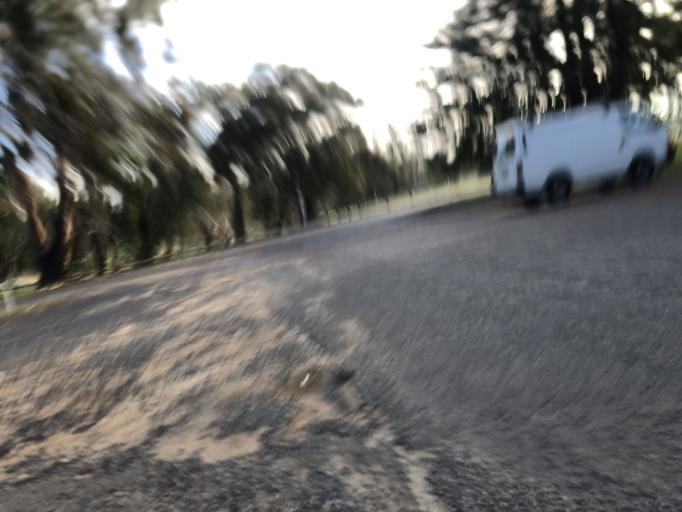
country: AU
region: New South Wales
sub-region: Orange Municipality
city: Orange
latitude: -33.3254
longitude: 149.0859
